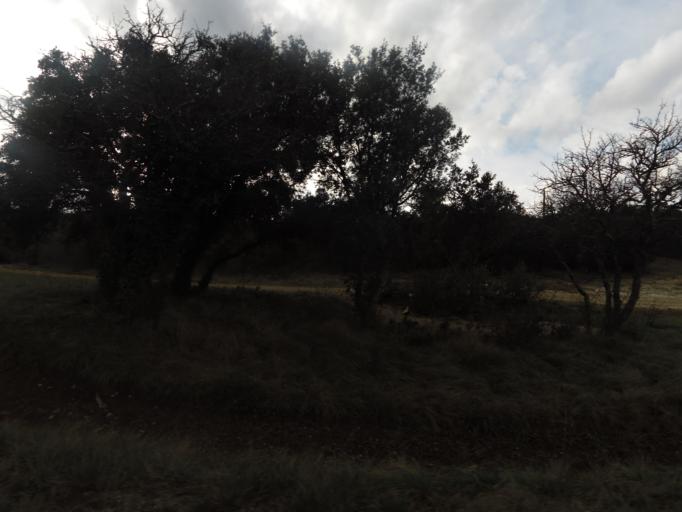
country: FR
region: Languedoc-Roussillon
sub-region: Departement du Gard
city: La Calmette
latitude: 43.8836
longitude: 4.2525
